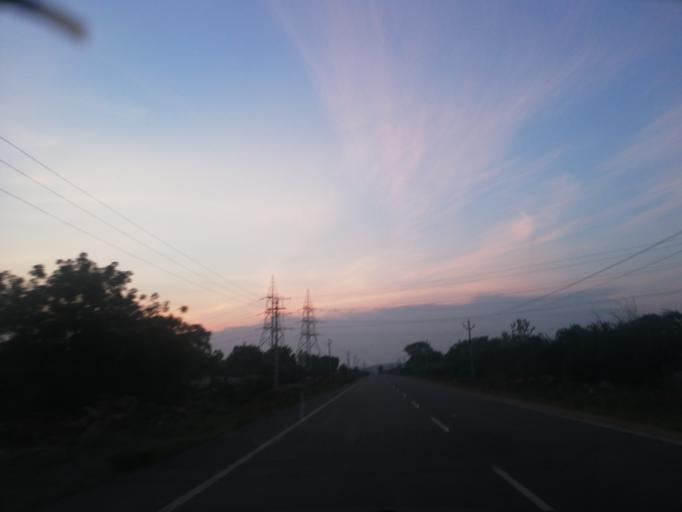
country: IN
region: Andhra Pradesh
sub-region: Guntur
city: Macherla
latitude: 16.6751
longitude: 79.2687
